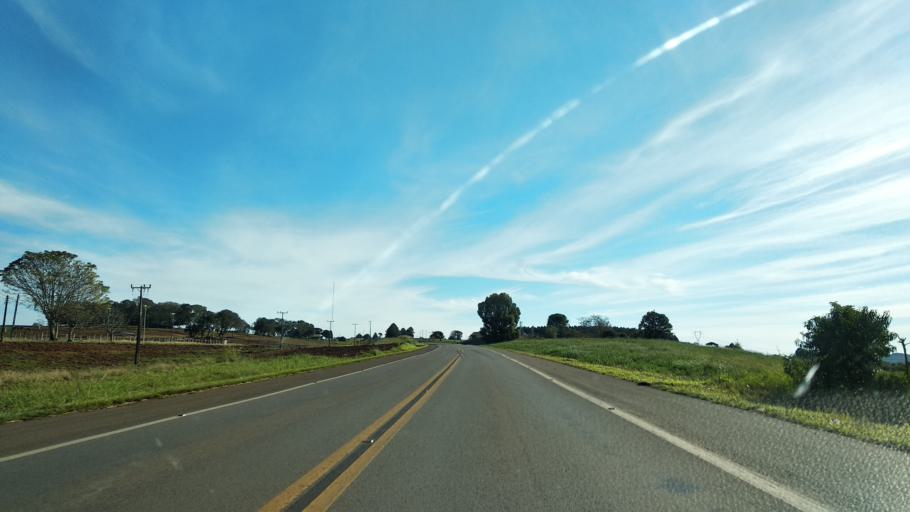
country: BR
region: Santa Catarina
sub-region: Celso Ramos
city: Celso Ramos
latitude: -27.5271
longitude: -51.3765
